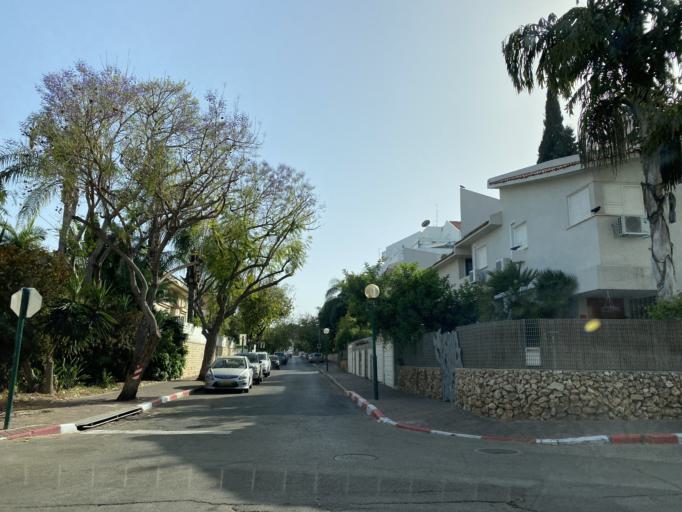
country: IL
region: Central District
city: Kfar Saba
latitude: 32.1867
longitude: 34.9024
